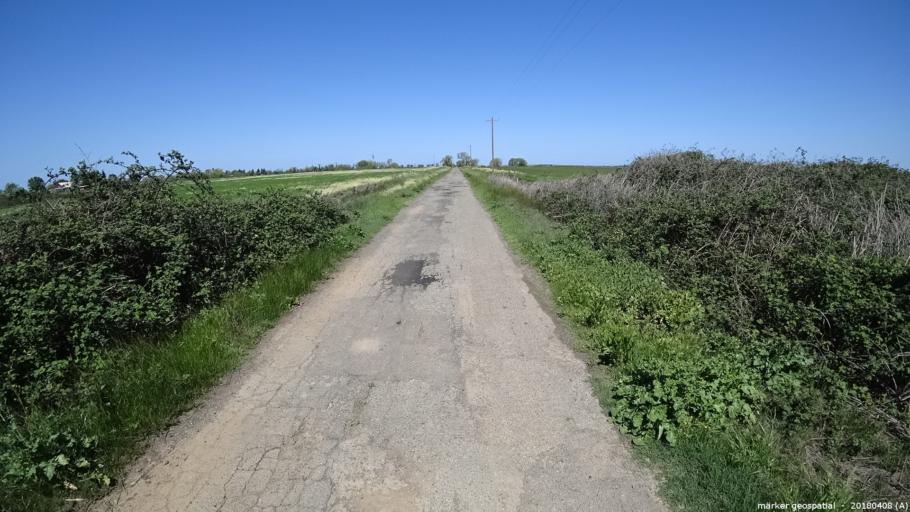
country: US
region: California
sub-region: Sacramento County
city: Laguna
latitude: 38.3584
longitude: -121.4822
